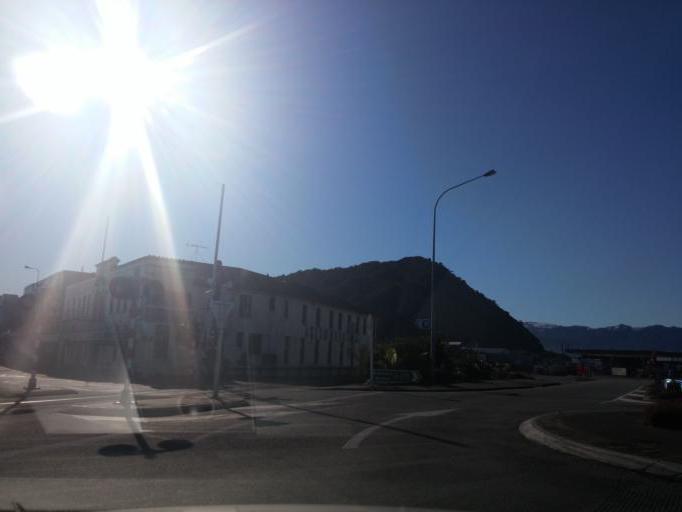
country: NZ
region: West Coast
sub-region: Grey District
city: Greymouth
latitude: -42.4501
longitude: 171.2110
